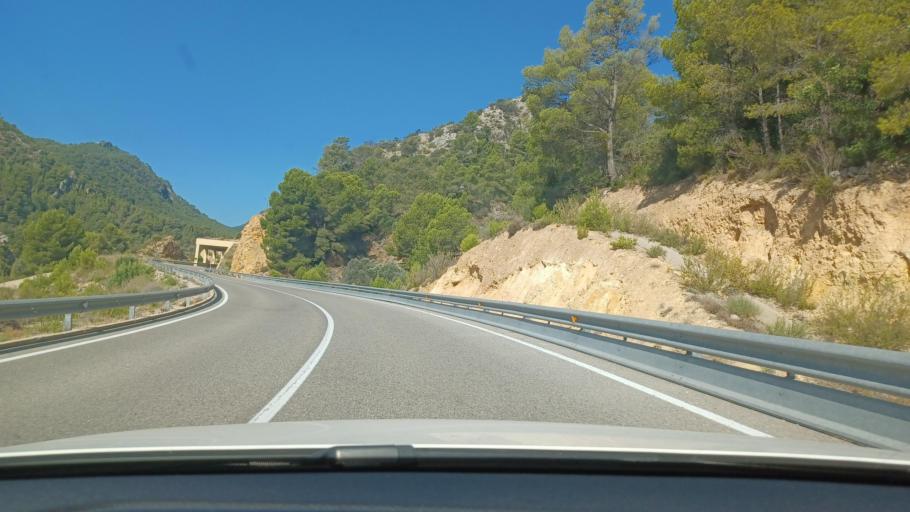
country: ES
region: Catalonia
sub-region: Provincia de Tarragona
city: Bot
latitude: 40.9721
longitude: 0.4414
